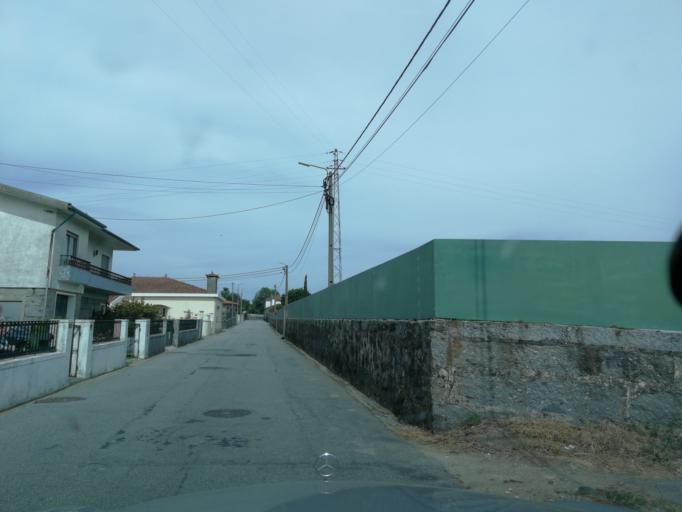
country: PT
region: Braga
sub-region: Vila Nova de Famalicao
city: Calendario
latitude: 41.4148
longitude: -8.5363
